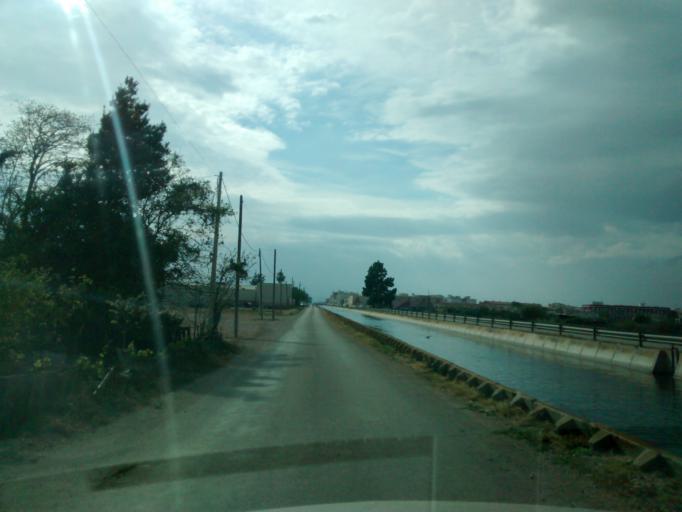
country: ES
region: Catalonia
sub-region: Provincia de Tarragona
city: Deltebre
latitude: 40.7023
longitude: 0.7260
